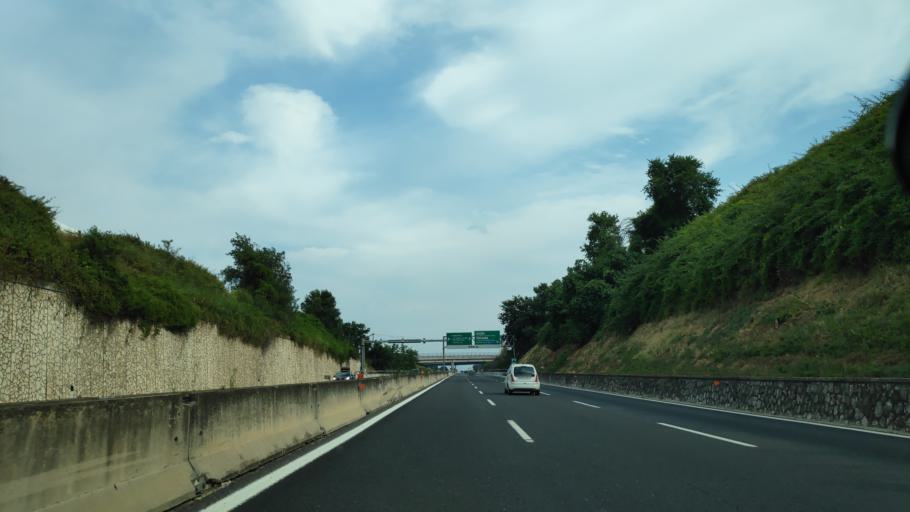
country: IT
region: Latium
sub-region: Citta metropolitana di Roma Capitale
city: Fiano Romano
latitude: 42.1773
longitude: 12.6043
